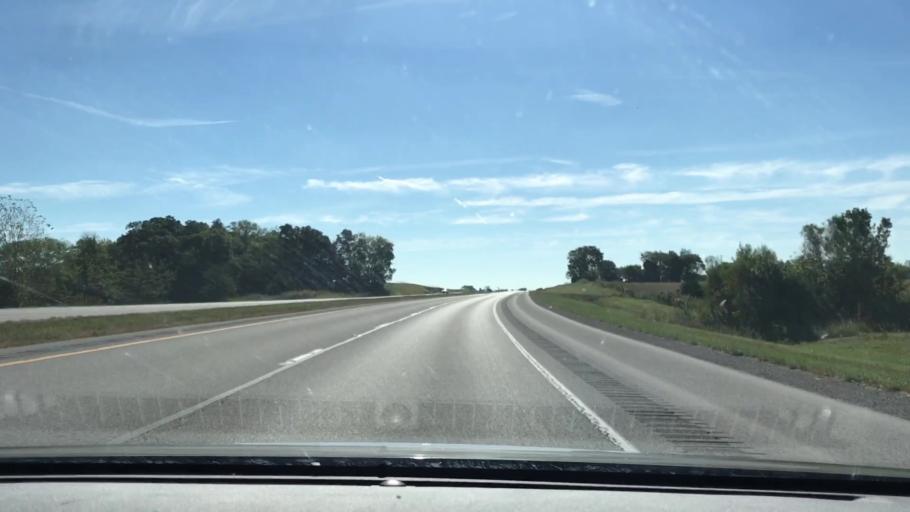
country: US
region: Kentucky
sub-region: Todd County
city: Elkton
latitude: 36.8213
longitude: -87.1456
